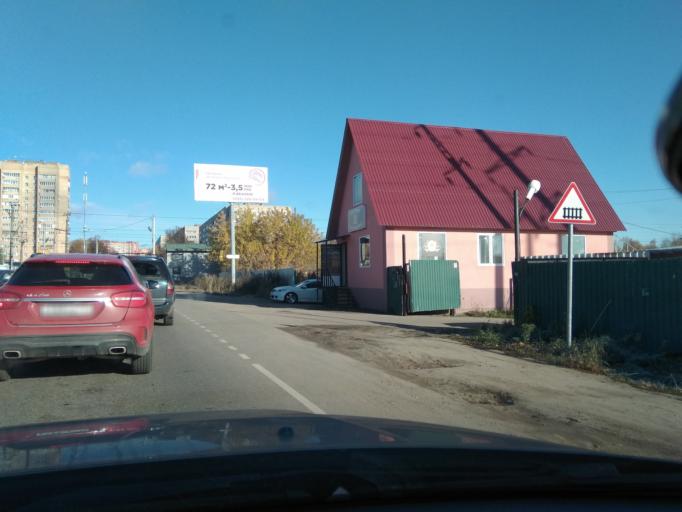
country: RU
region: Moskovskaya
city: Istra
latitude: 55.9026
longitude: 36.8586
